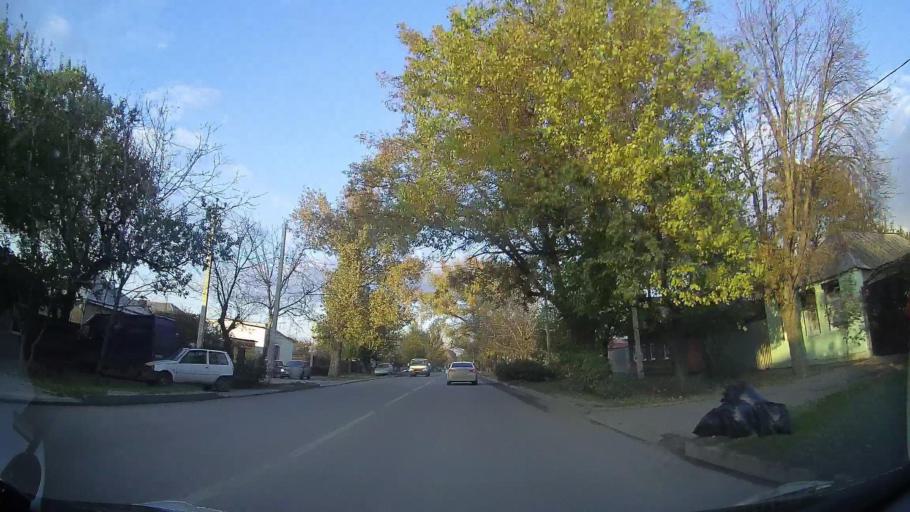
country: RU
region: Rostov
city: Imeni Chkalova
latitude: 47.2673
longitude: 39.7783
